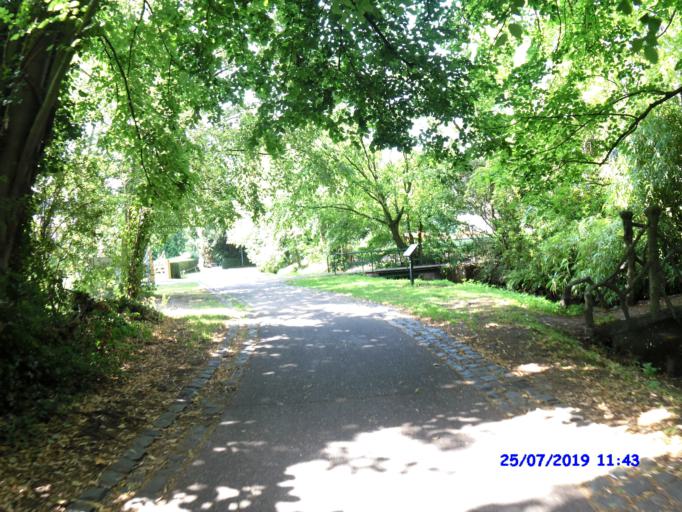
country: BE
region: Flanders
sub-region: Provincie Antwerpen
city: Mol
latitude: 51.1853
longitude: 5.1194
